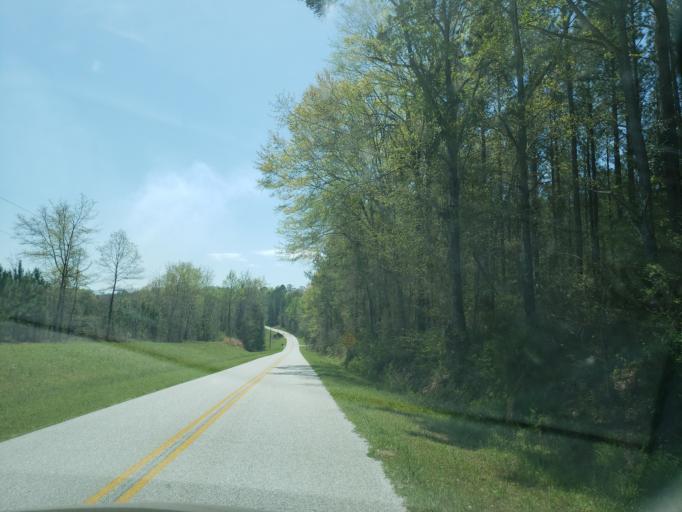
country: US
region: Alabama
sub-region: Elmore County
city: Tallassee
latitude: 32.6754
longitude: -85.8624
